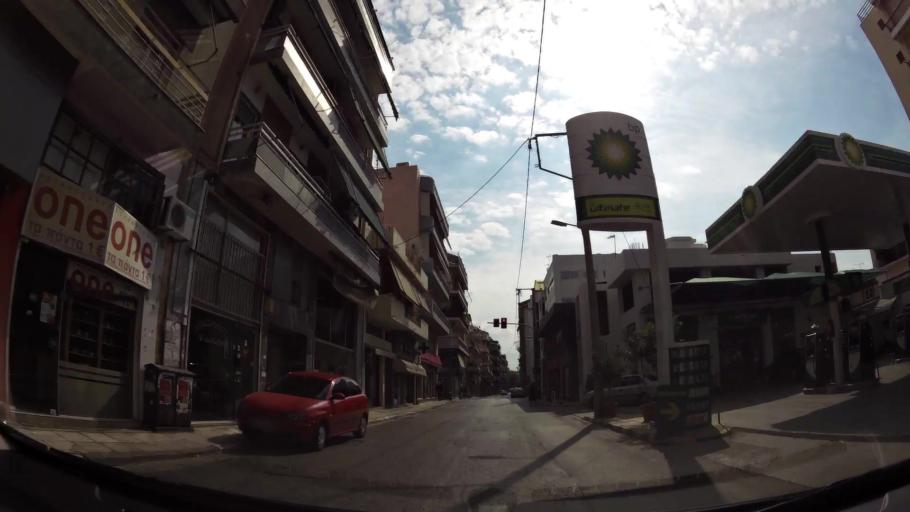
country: GR
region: Attica
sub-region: Nomarchia Athinas
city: Athens
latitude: 37.9909
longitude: 23.7108
